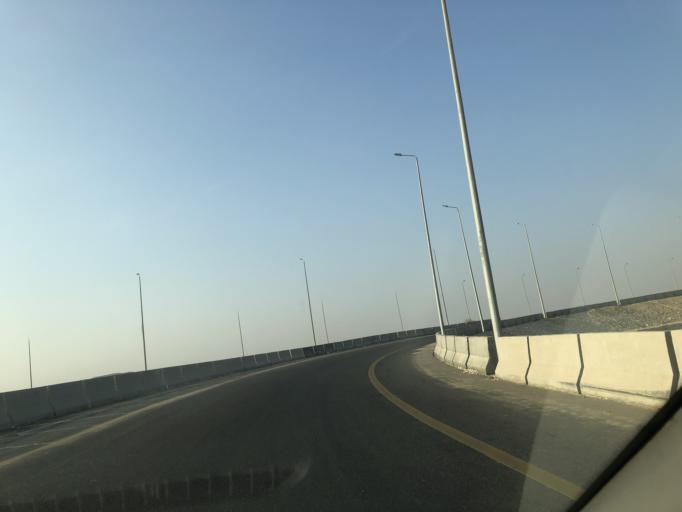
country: EG
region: Al Jizah
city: Madinat Sittah Uktubar
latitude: 29.8920
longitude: 31.0032
